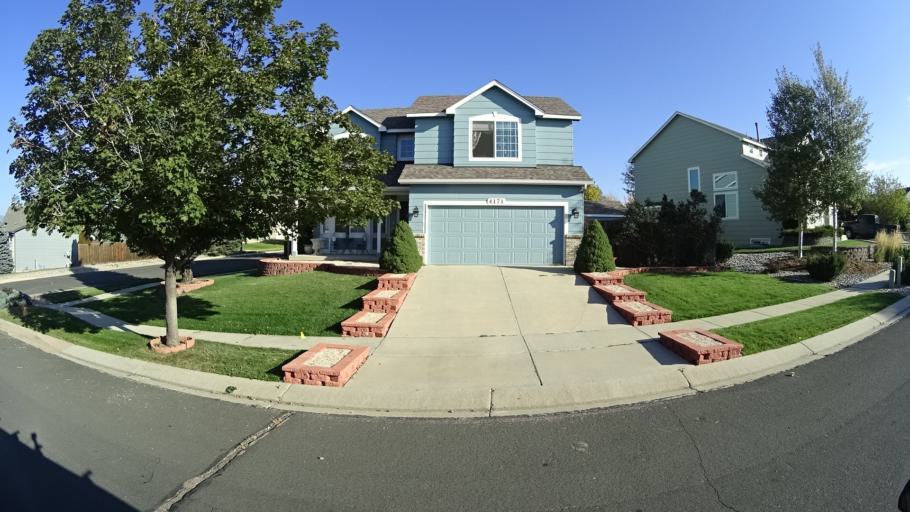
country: US
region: Colorado
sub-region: El Paso County
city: Cimarron Hills
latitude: 38.8901
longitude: -104.7001
